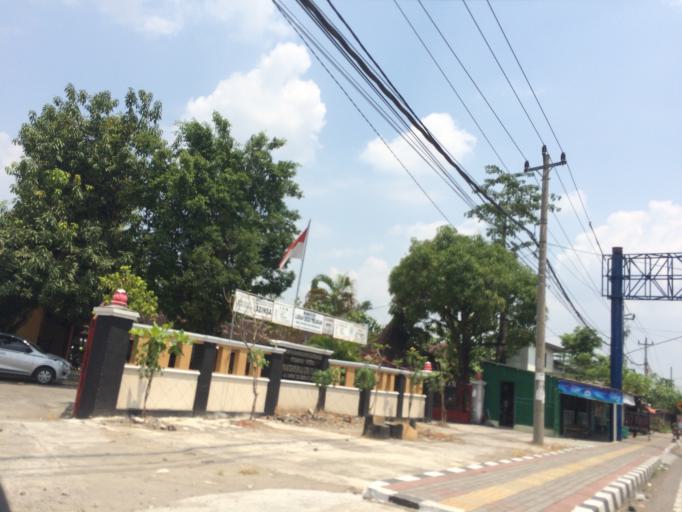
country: ID
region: Central Java
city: Grogol
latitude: -7.6199
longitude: 110.8209
